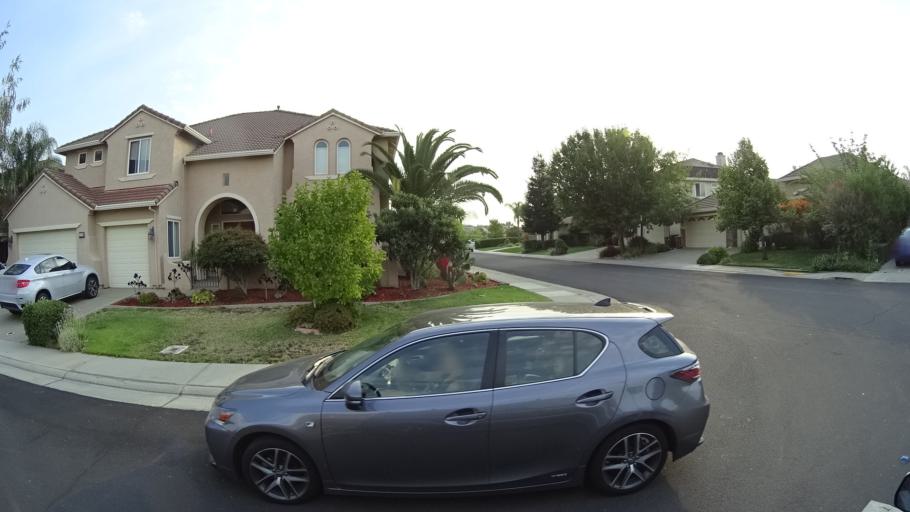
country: US
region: California
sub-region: Sacramento County
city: Laguna
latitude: 38.3812
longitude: -121.4213
